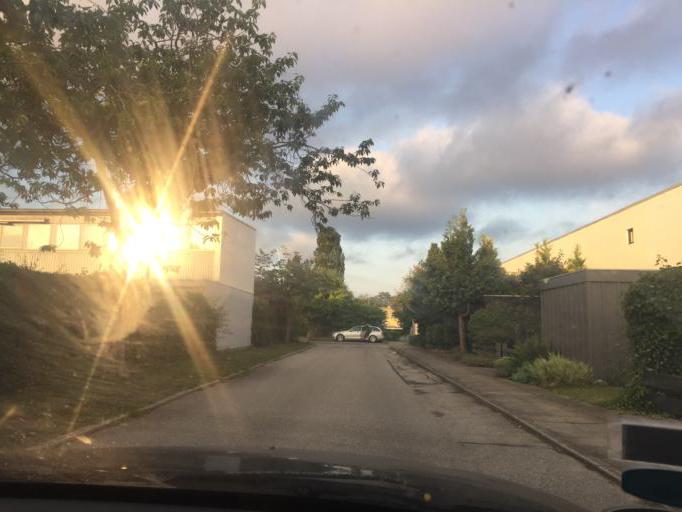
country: DK
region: Capital Region
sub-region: Albertslund Kommune
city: Albertslund
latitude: 55.6730
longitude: 12.3667
